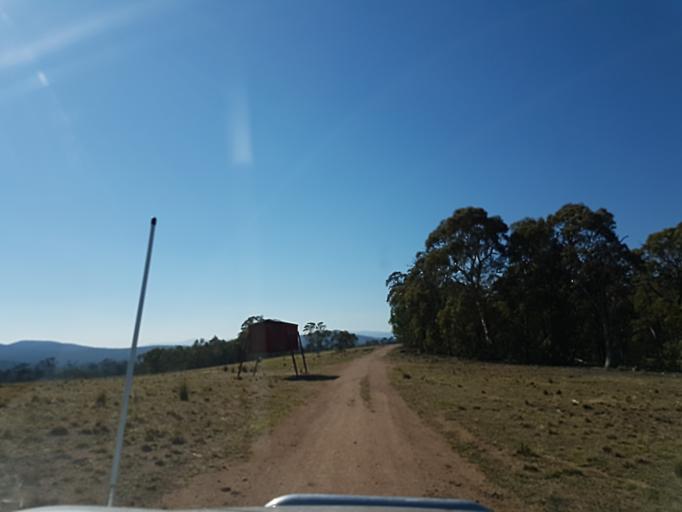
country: AU
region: New South Wales
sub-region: Snowy River
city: Jindabyne
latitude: -37.0385
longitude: 148.2808
